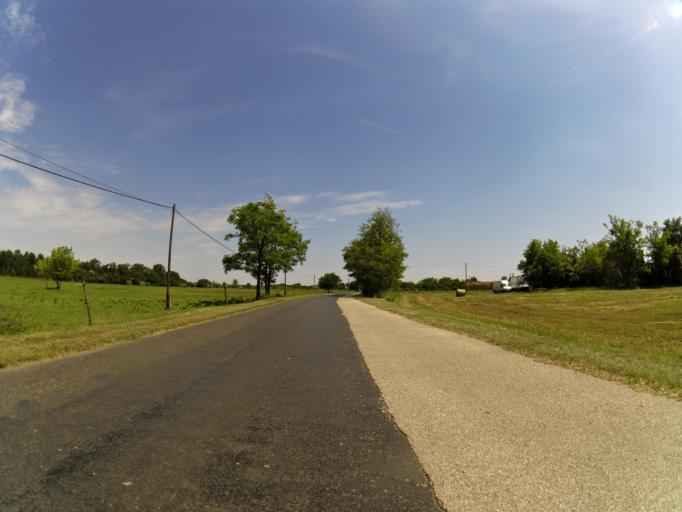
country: HU
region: Csongrad
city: Szatymaz
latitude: 46.3568
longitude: 20.0221
